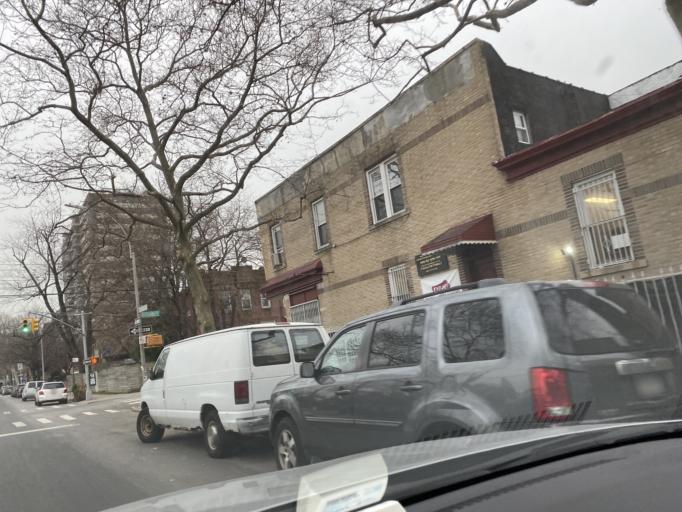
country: US
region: New York
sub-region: Kings County
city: Brooklyn
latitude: 40.6601
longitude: -73.9454
